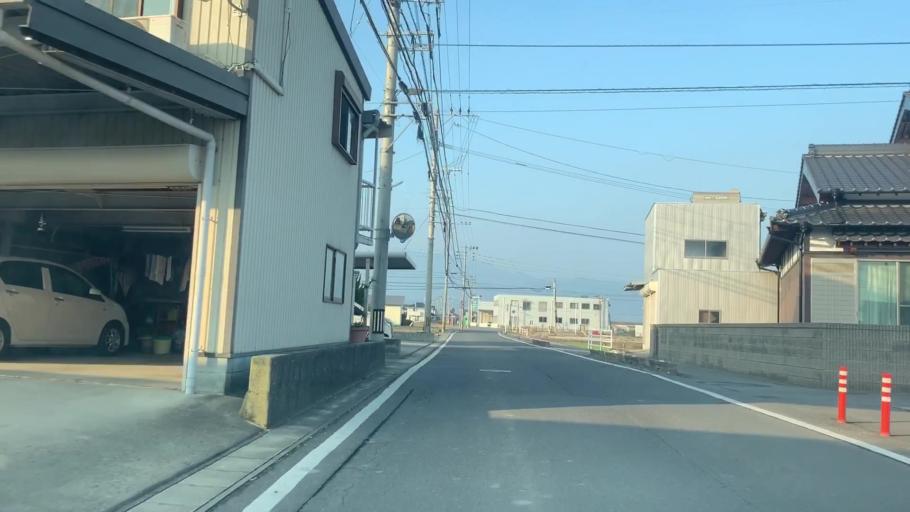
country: JP
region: Saga Prefecture
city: Saga-shi
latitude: 33.2658
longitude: 130.2307
